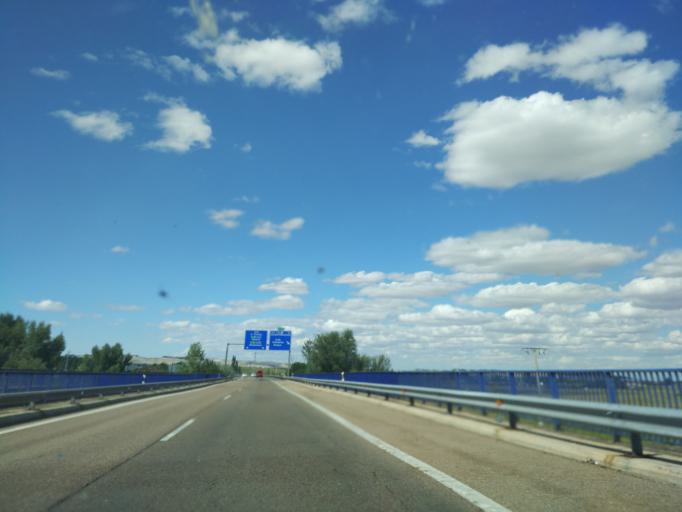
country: ES
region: Castille and Leon
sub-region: Provincia de Valladolid
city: Tordesillas
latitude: 41.4901
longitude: -4.9841
